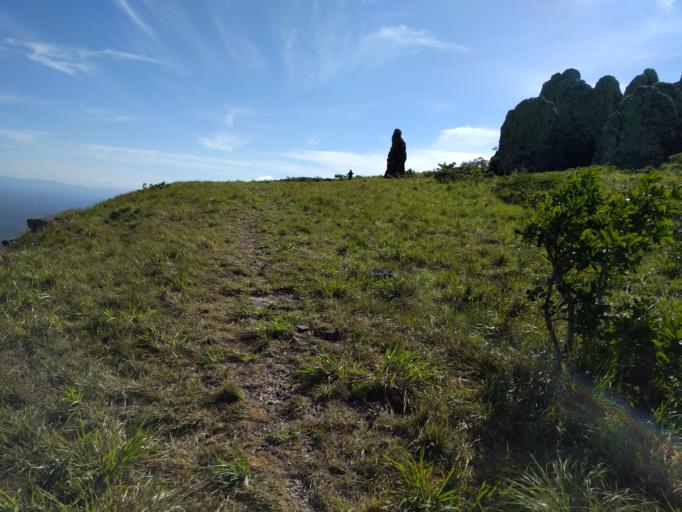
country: BO
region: Santa Cruz
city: Robore
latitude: -18.3227
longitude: -59.5725
